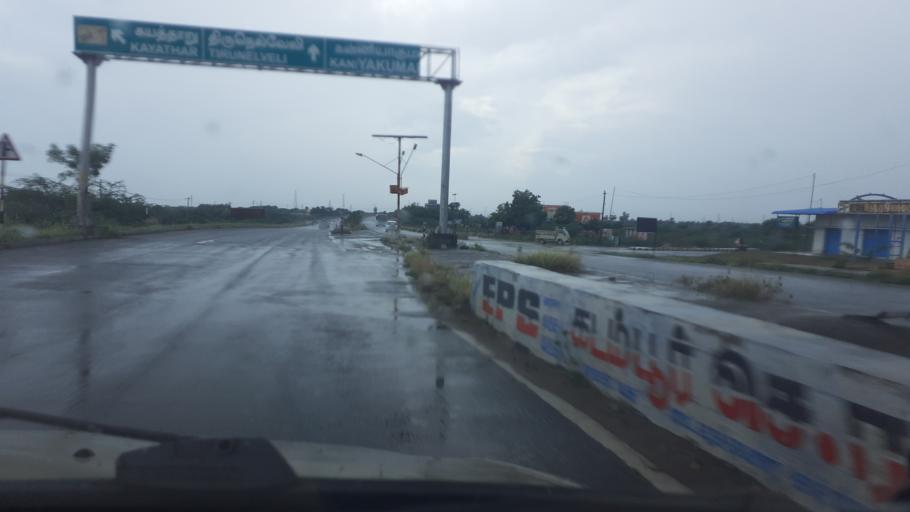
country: IN
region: Tamil Nadu
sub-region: Thoothukkudi
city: Kayattar
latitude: 8.9656
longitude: 77.7734
